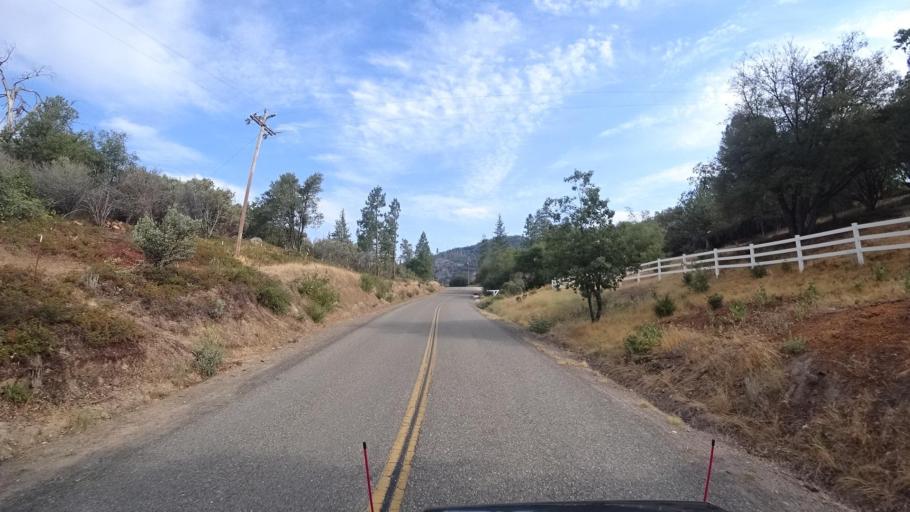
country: US
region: California
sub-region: Madera County
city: Ahwahnee
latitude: 37.4736
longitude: -119.7723
